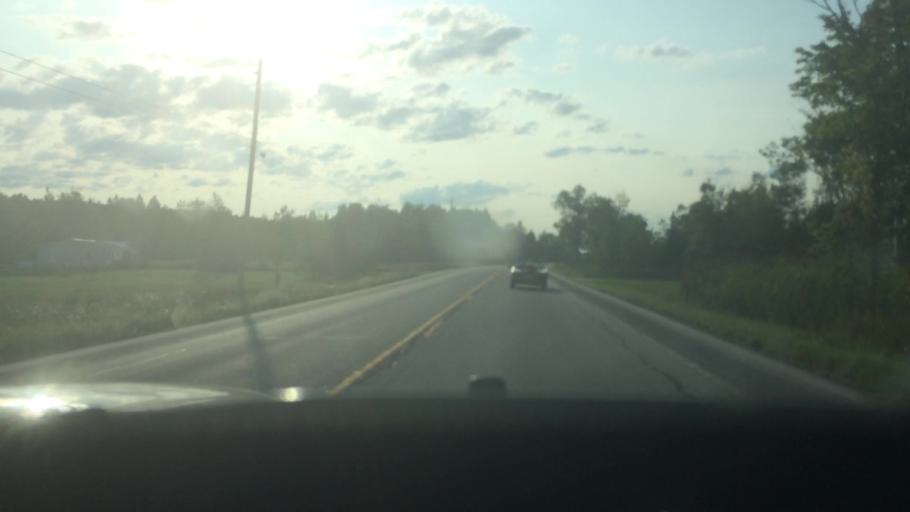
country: US
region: New York
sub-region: St. Lawrence County
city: Canton
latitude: 44.6572
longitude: -75.3222
